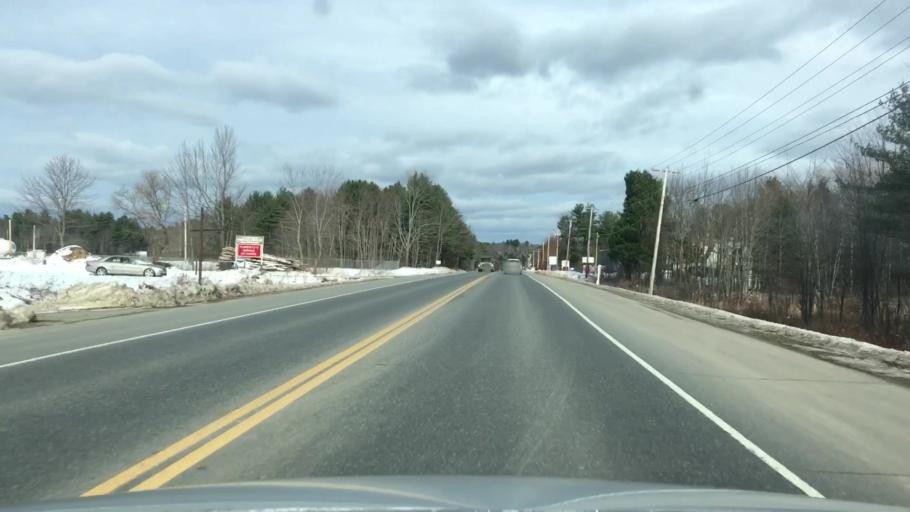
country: US
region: Maine
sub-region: Kennebec County
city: Winthrop
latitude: 44.2846
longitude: -69.9995
